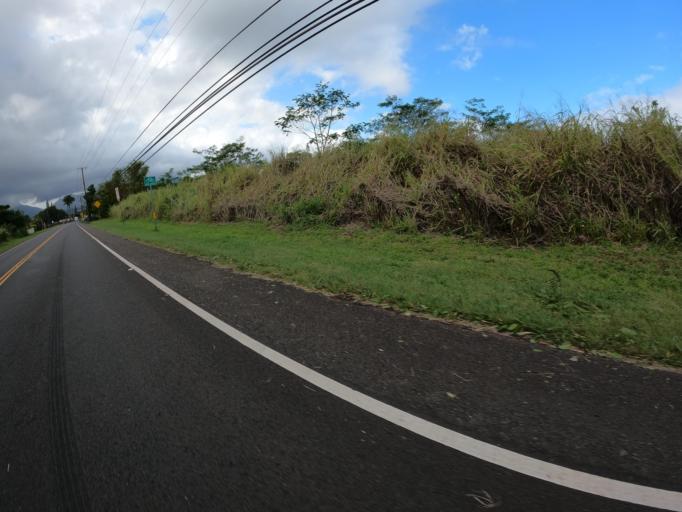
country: US
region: Hawaii
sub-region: Honolulu County
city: Whitmore Village
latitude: 21.5118
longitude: -158.0169
